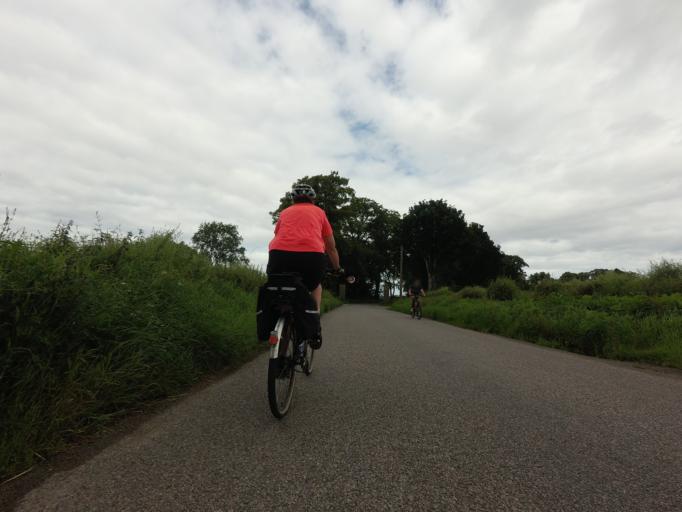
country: GB
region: Scotland
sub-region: Moray
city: Forres
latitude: 57.6167
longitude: -3.6535
